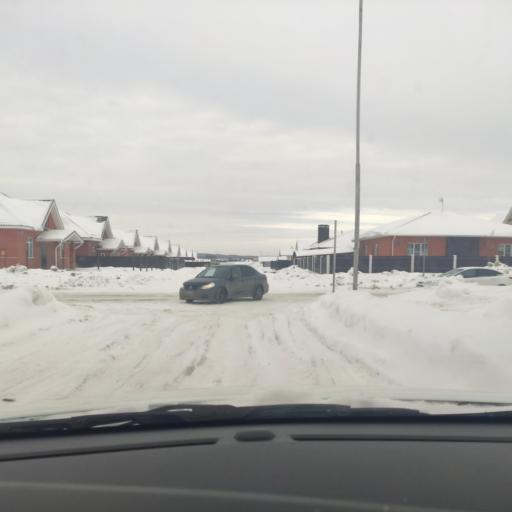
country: RU
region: Tatarstan
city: Stolbishchi
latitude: 55.7081
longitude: 49.3442
